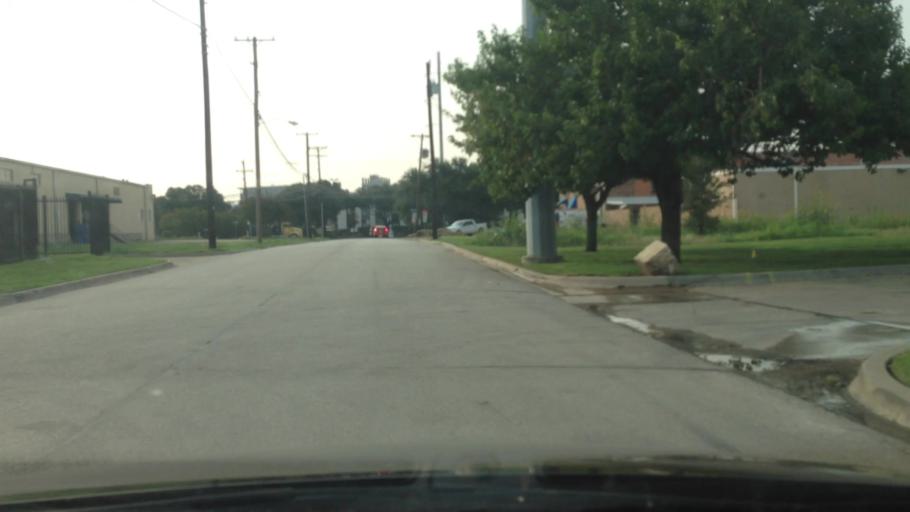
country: US
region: Texas
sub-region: Dallas County
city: Irving
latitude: 32.8249
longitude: -96.8779
